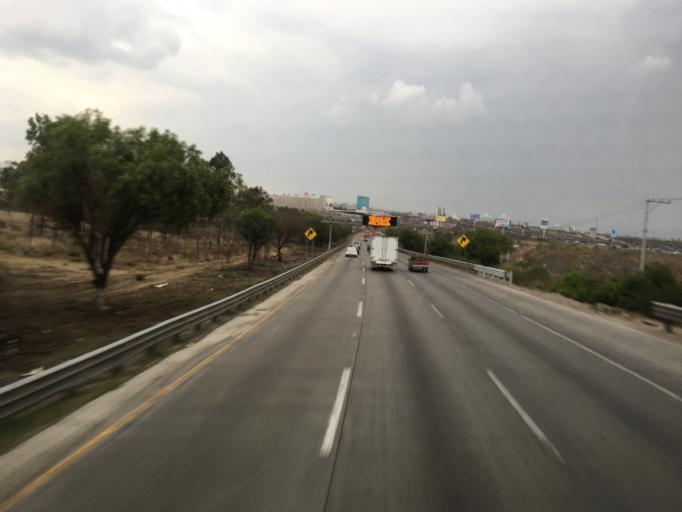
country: MX
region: Queretaro
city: La Canada
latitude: 20.5758
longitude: -100.3314
